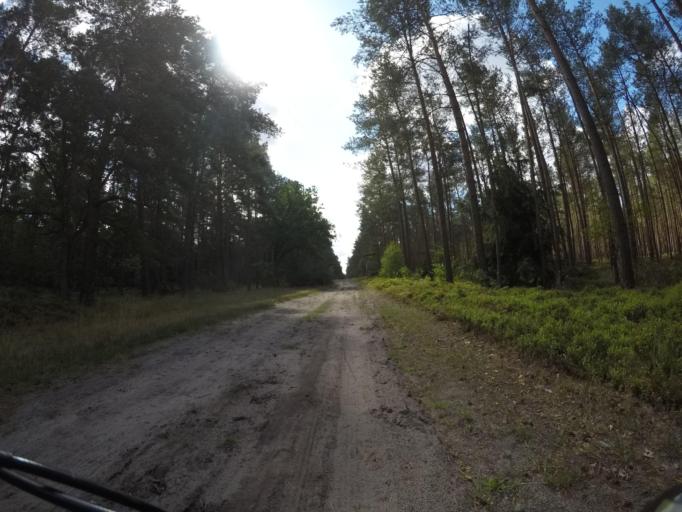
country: DE
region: Lower Saxony
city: Hitzacker
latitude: 53.2300
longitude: 11.0274
